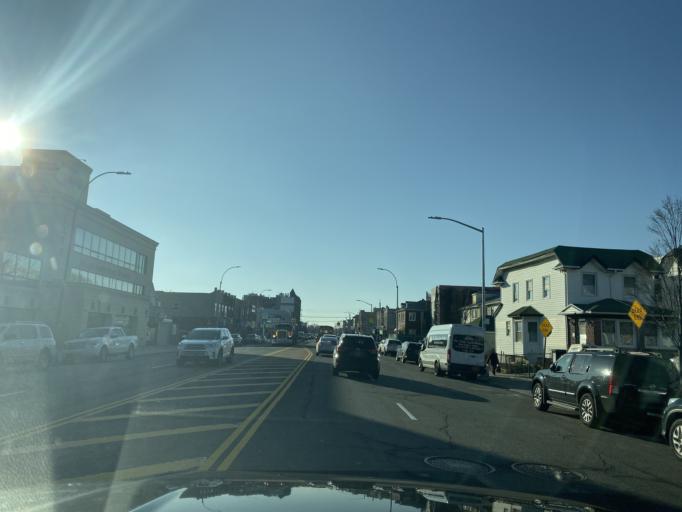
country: US
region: New York
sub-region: Kings County
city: Bensonhurst
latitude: 40.6020
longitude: -73.9615
